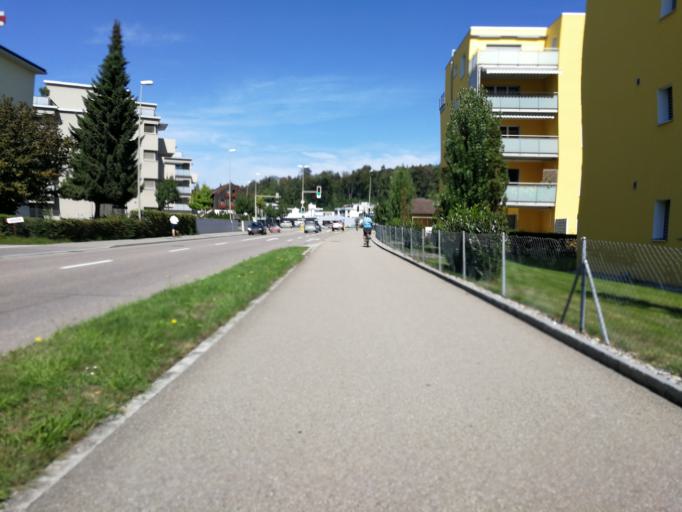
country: CH
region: Zurich
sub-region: Bezirk Hinwil
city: Wetzikon / Kempten
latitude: 47.3343
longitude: 8.8121
